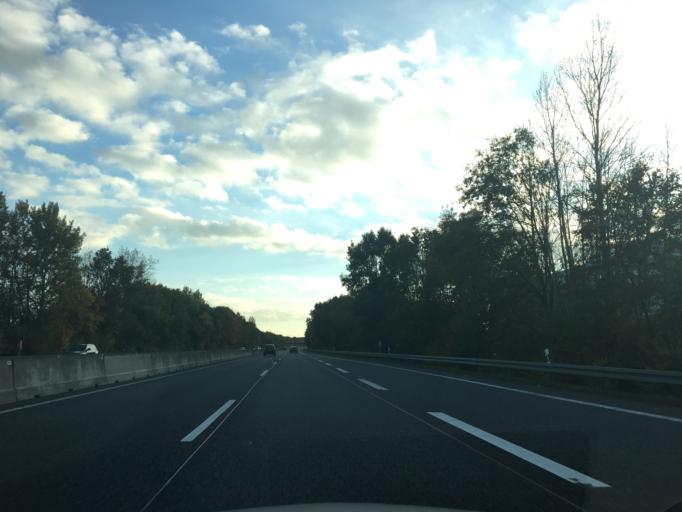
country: DE
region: Hesse
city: Dreieich
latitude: 50.0283
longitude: 8.7112
